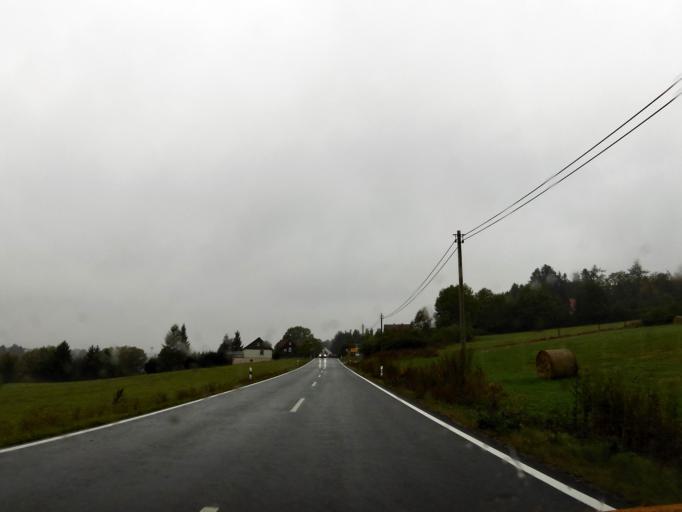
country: DE
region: Saxony-Anhalt
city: Hasselfelde
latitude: 51.6647
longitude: 10.8968
